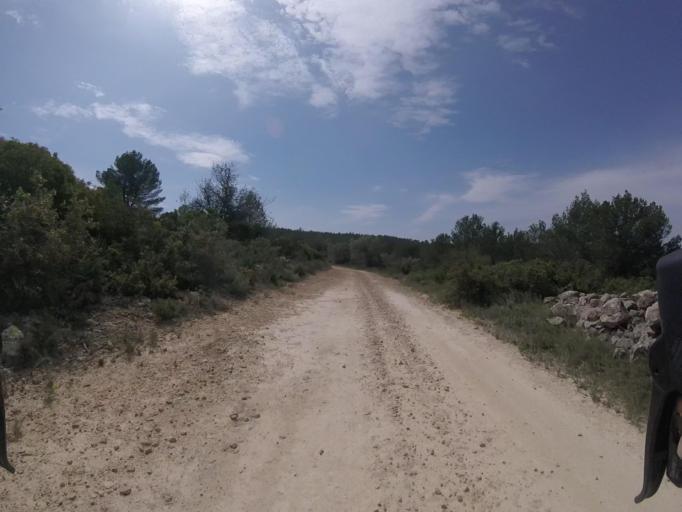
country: ES
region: Valencia
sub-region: Provincia de Castello
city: Cuevas de Vinroma
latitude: 40.2819
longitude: 0.1235
